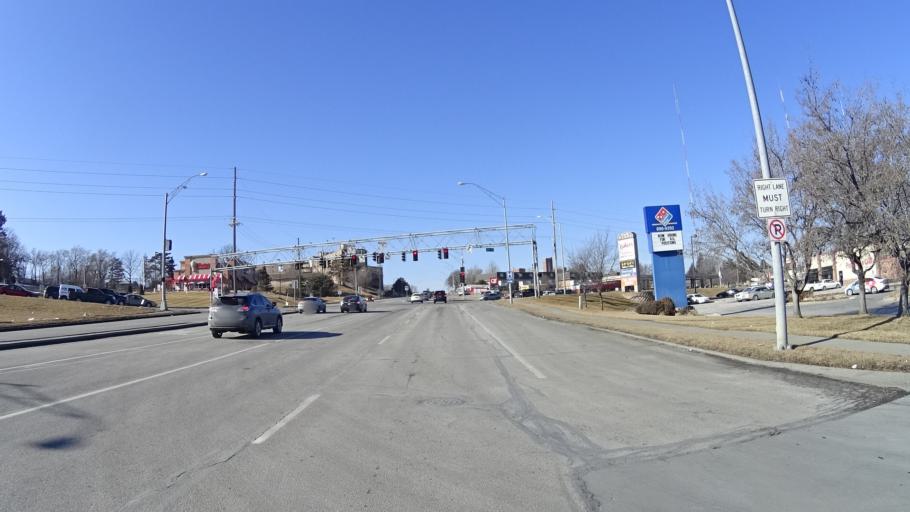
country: US
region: Nebraska
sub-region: Douglas County
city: Omaha
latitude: 41.2973
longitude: -96.0229
